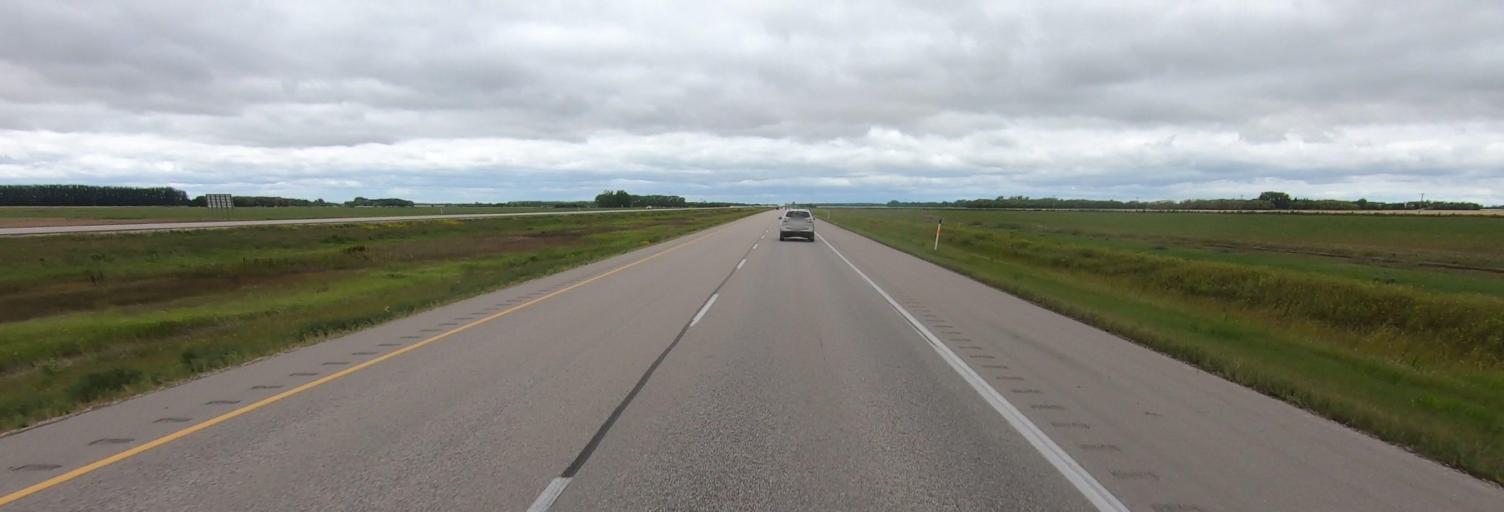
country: CA
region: Manitoba
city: Portage la Prairie
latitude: 49.9426
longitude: -97.9495
